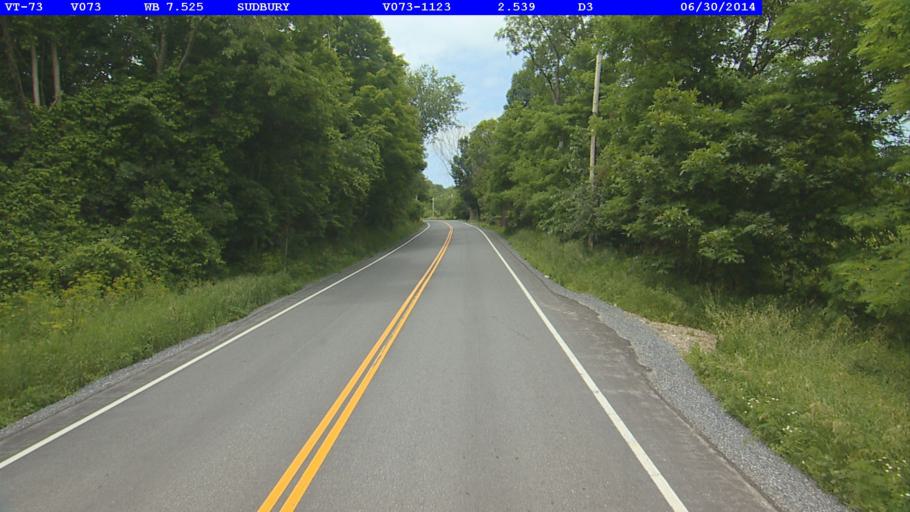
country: US
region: Vermont
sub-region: Rutland County
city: Brandon
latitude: 43.8128
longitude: -73.1571
